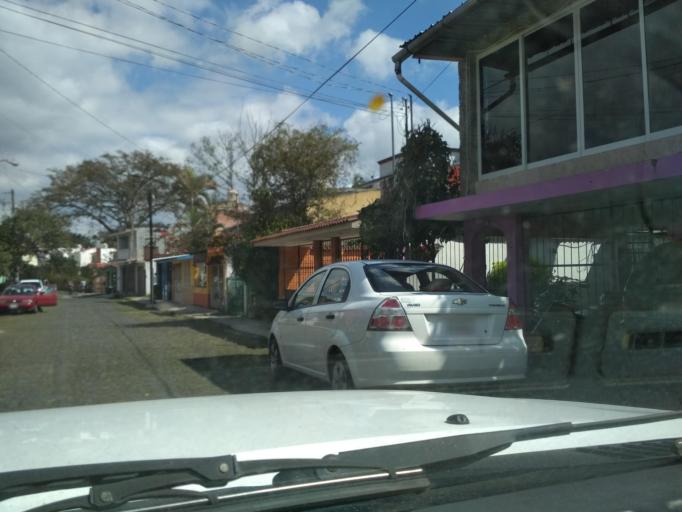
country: MX
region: Veracruz
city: Coatepec
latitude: 19.4502
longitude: -96.9494
